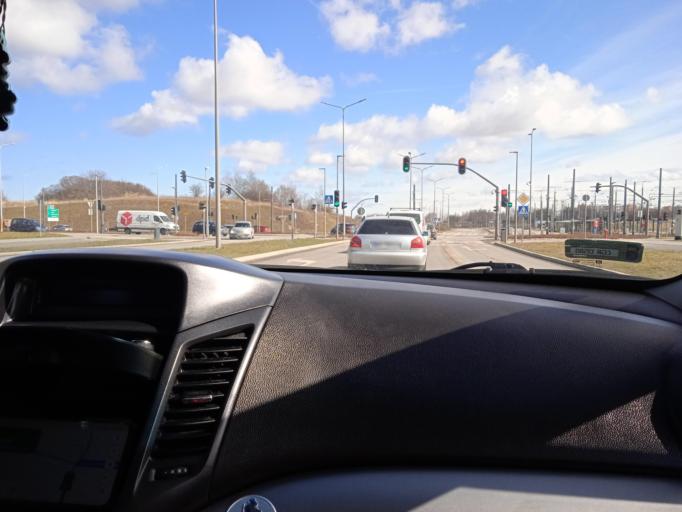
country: PL
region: Pomeranian Voivodeship
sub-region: Powiat gdanski
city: Kowale
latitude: 54.3320
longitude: 18.5686
